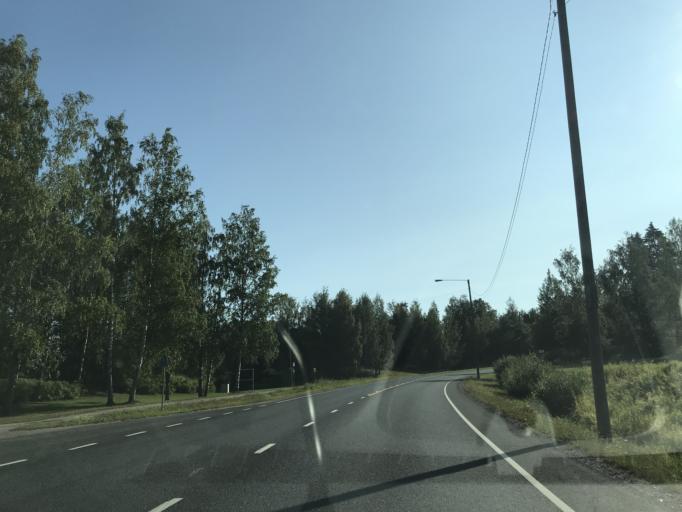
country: FI
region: Paijanne Tavastia
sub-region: Lahti
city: Orimattila
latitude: 60.7950
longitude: 25.7007
